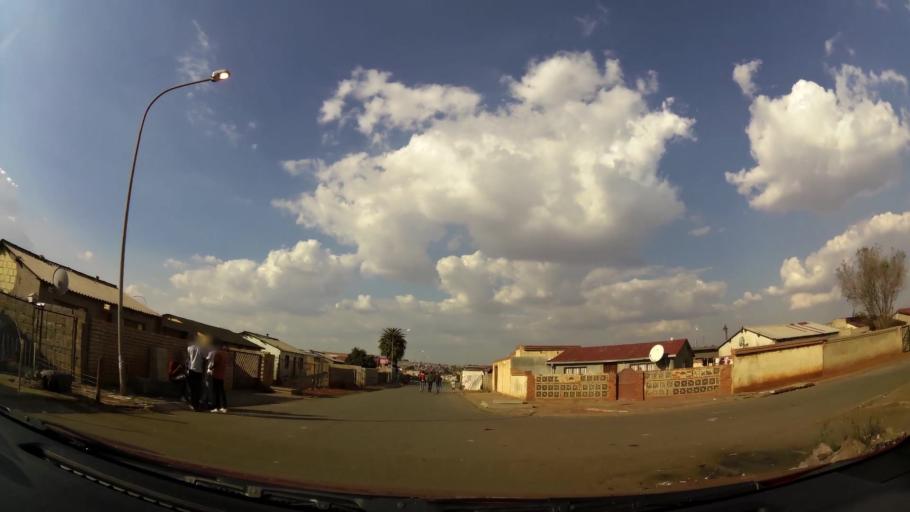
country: ZA
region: Gauteng
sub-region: City of Johannesburg Metropolitan Municipality
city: Soweto
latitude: -26.2237
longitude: 27.8674
